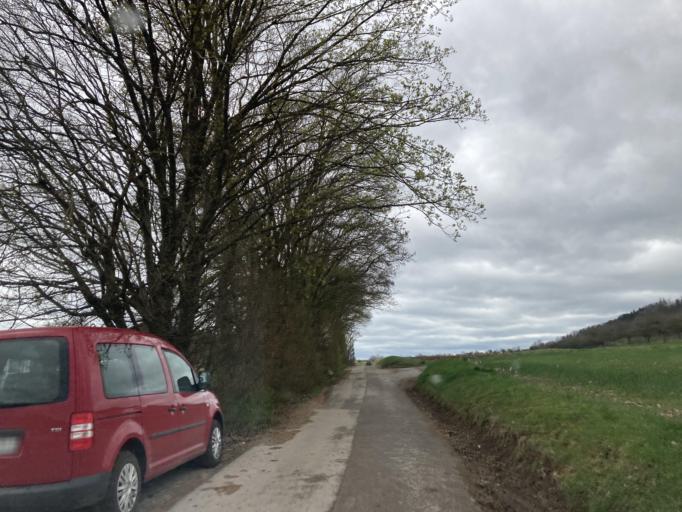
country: DE
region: Baden-Wuerttemberg
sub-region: Tuebingen Region
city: Rottenburg
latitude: 48.5206
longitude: 8.9679
